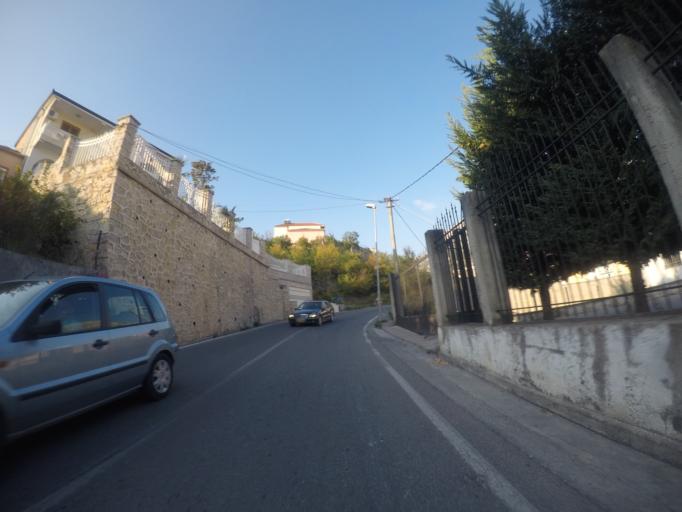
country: AL
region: Durres
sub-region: Rrethi i Krujes
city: Kruje
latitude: 41.5097
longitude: 19.7837
